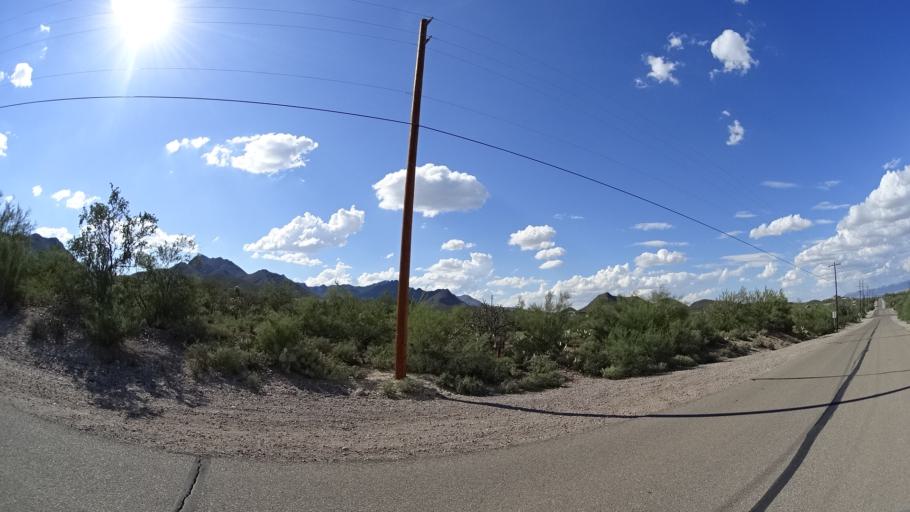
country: US
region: Arizona
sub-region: Pima County
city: Tucson Estates
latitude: 32.2341
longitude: -111.0627
